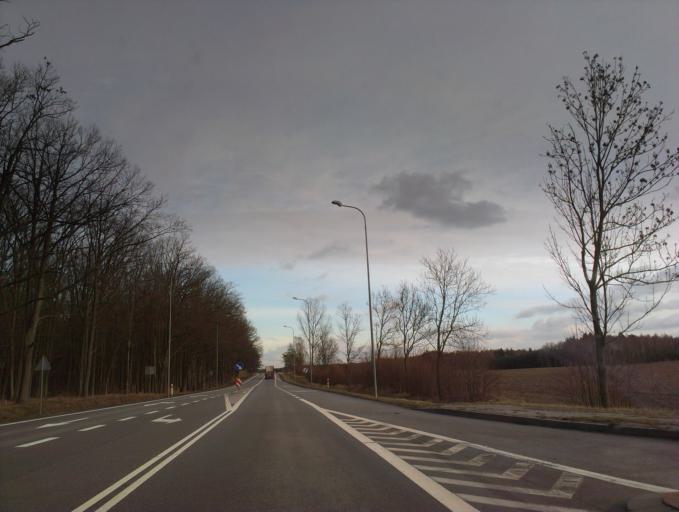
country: PL
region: Kujawsko-Pomorskie
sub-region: Powiat lipnowski
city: Skepe
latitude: 52.8576
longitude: 19.2864
